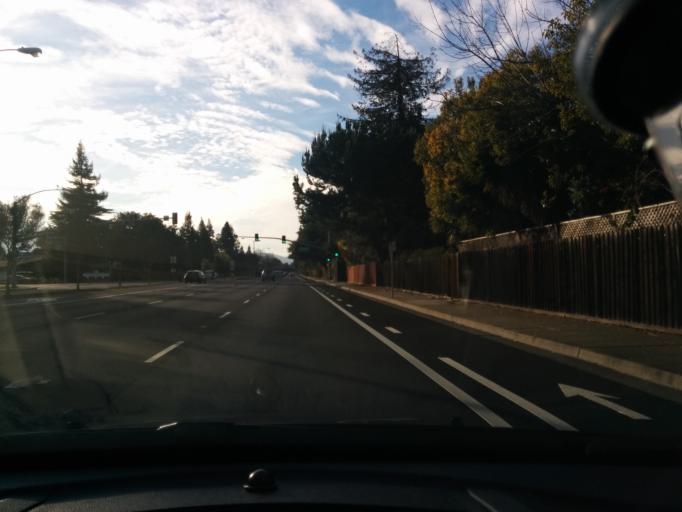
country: US
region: California
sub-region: Santa Clara County
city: Sunnyvale
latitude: 37.3522
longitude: -122.0540
